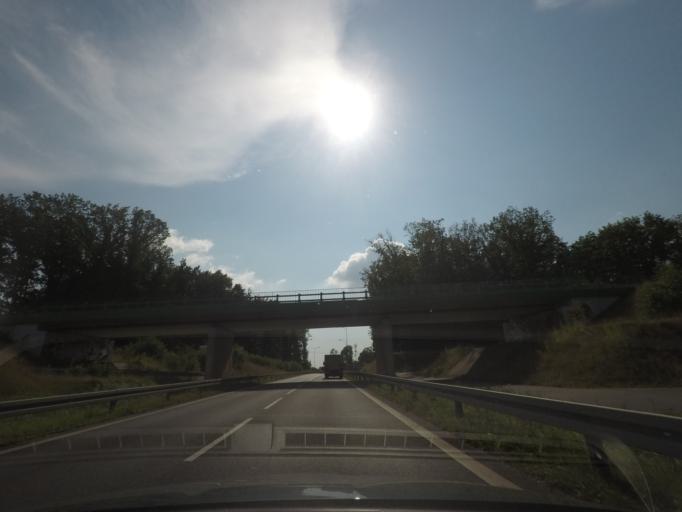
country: PL
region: Silesian Voivodeship
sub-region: Powiat pszczynski
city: Radostowice
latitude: 49.9988
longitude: 18.8982
